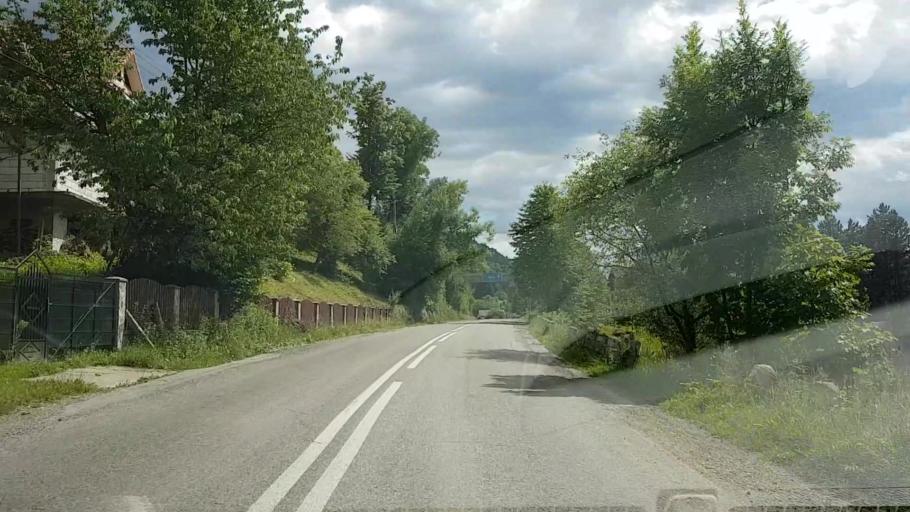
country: RO
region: Neamt
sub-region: Comuna Poiana Teiului
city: Poiana Teiului
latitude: 47.0865
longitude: 25.9705
